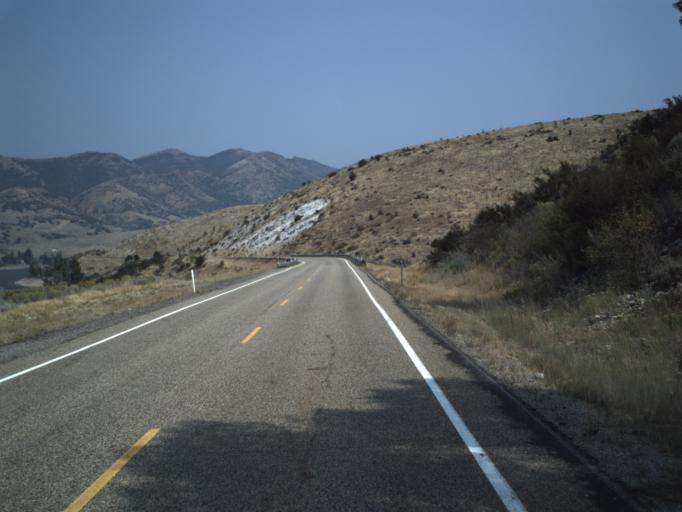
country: US
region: Utah
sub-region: Morgan County
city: Morgan
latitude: 40.9061
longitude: -111.5872
